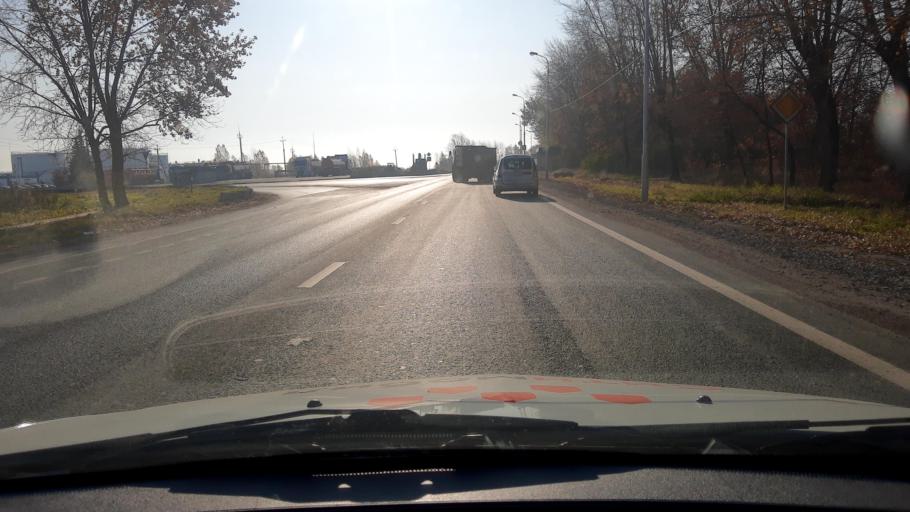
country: RU
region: Bashkortostan
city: Ufa
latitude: 54.8615
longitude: 56.1106
